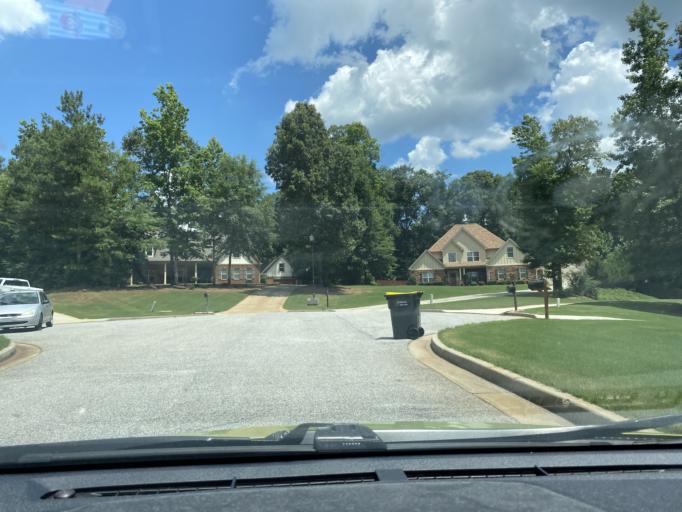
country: US
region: Georgia
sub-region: Fayette County
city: Peachtree City
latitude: 33.4308
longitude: -84.6717
